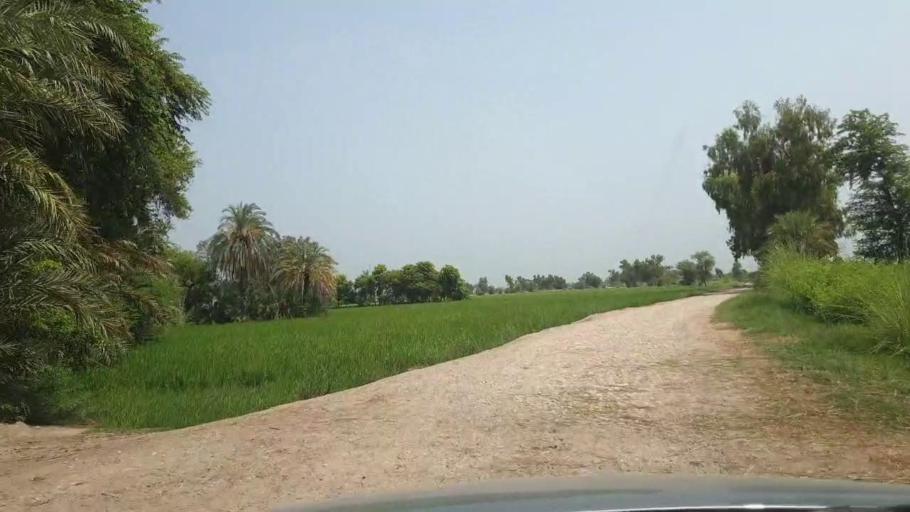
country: PK
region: Sindh
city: Madeji
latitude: 27.7938
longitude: 68.5301
